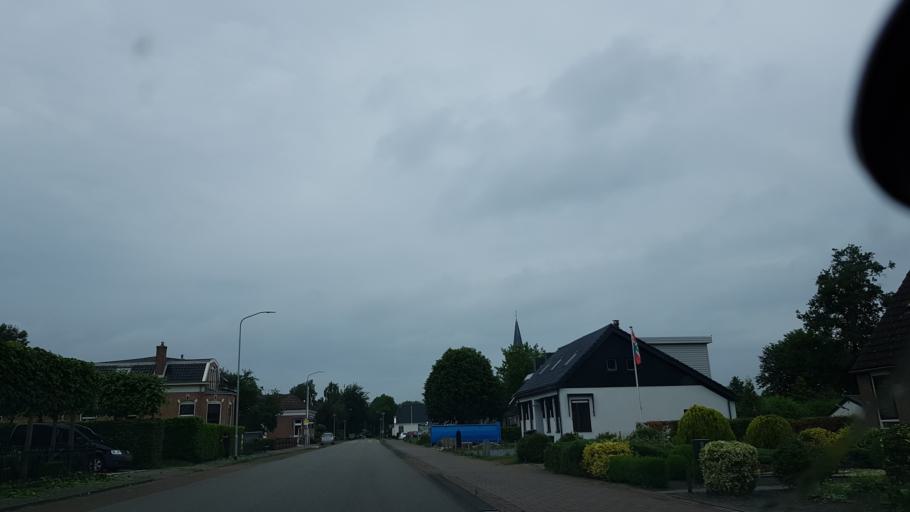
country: NL
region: Groningen
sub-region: Gemeente Hoogezand-Sappemeer
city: Hoogezand
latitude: 53.1474
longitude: 6.7237
